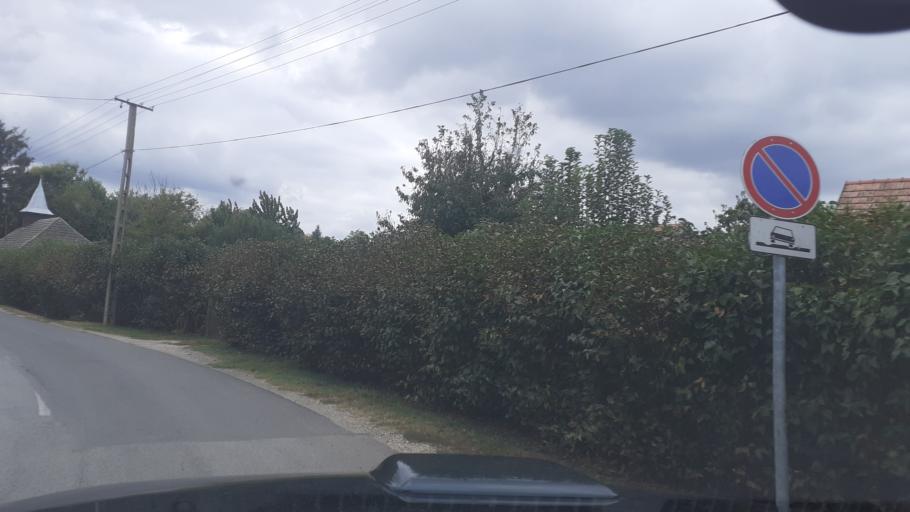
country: HU
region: Fejer
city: Racalmas
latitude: 47.0530
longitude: 18.9190
